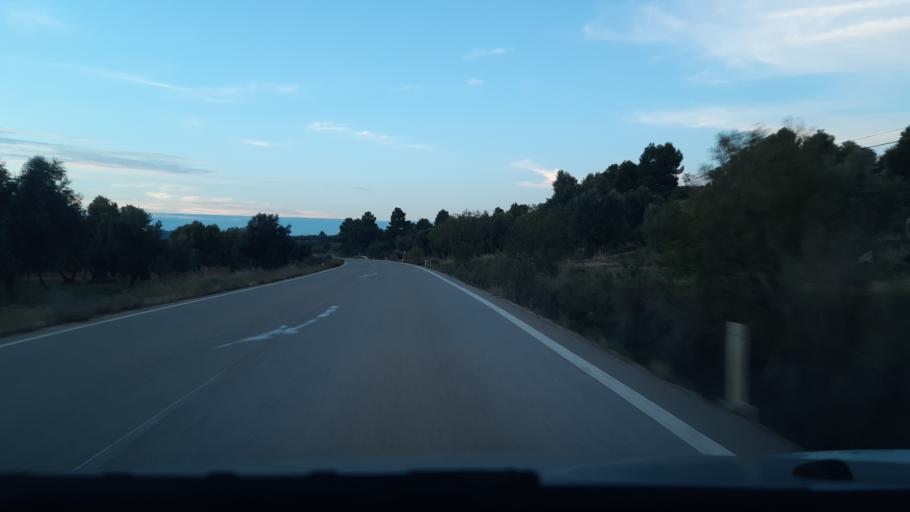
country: ES
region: Aragon
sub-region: Provincia de Teruel
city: Valderrobres
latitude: 40.8540
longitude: 0.1729
